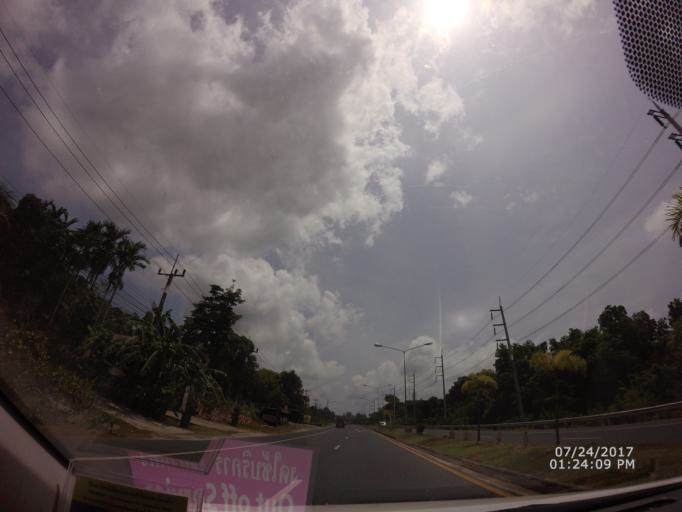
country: TH
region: Phuket
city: Thalang
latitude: 8.0904
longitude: 98.3280
